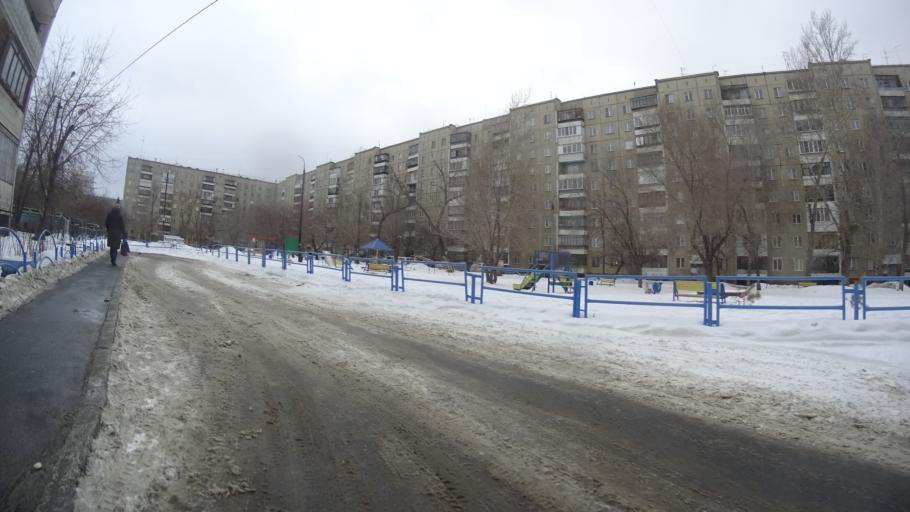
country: RU
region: Chelyabinsk
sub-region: Gorod Chelyabinsk
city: Chelyabinsk
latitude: 55.1775
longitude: 61.3396
